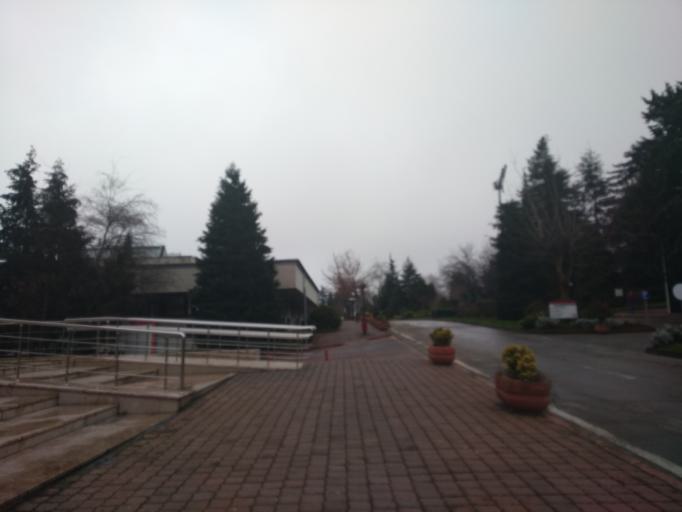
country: TR
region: Trabzon
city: Trabzon
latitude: 40.9978
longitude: 39.7699
